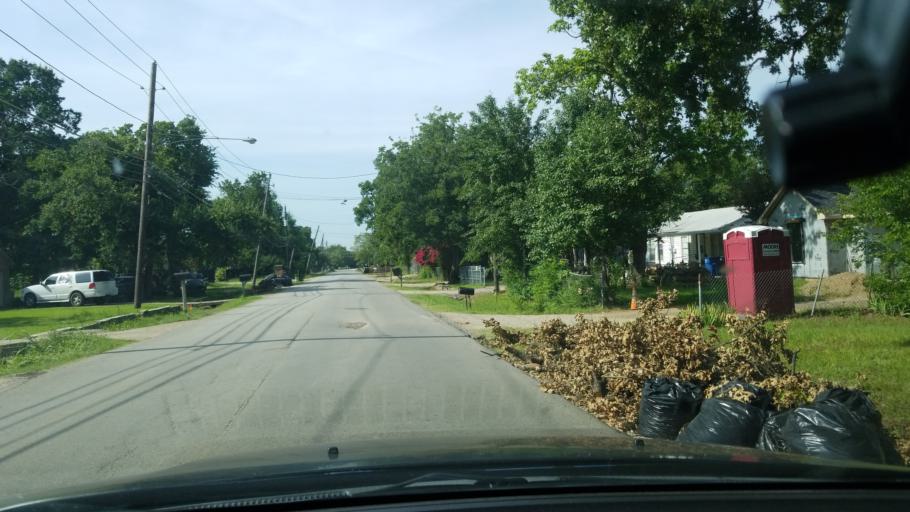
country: US
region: Texas
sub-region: Dallas County
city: Balch Springs
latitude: 32.7224
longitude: -96.6393
